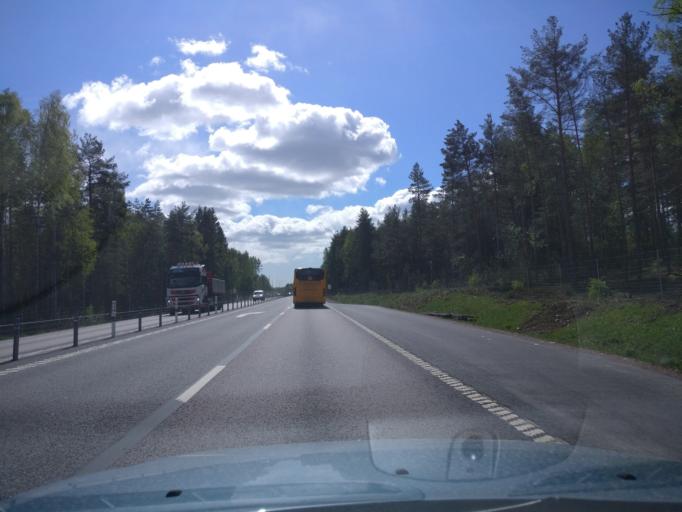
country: SE
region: Vaermland
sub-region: Karlstads Kommun
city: Karlstad
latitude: 59.4121
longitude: 13.5321
